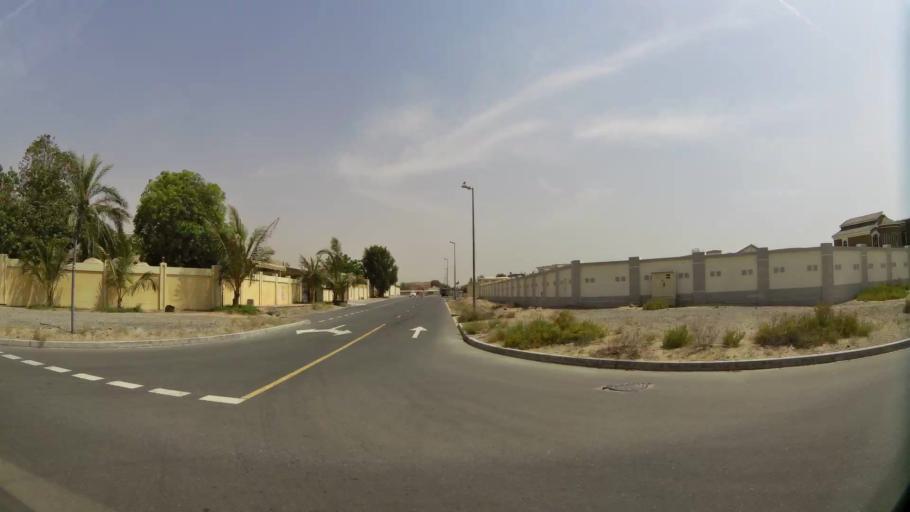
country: AE
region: Ash Shariqah
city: Sharjah
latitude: 25.2595
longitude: 55.4727
